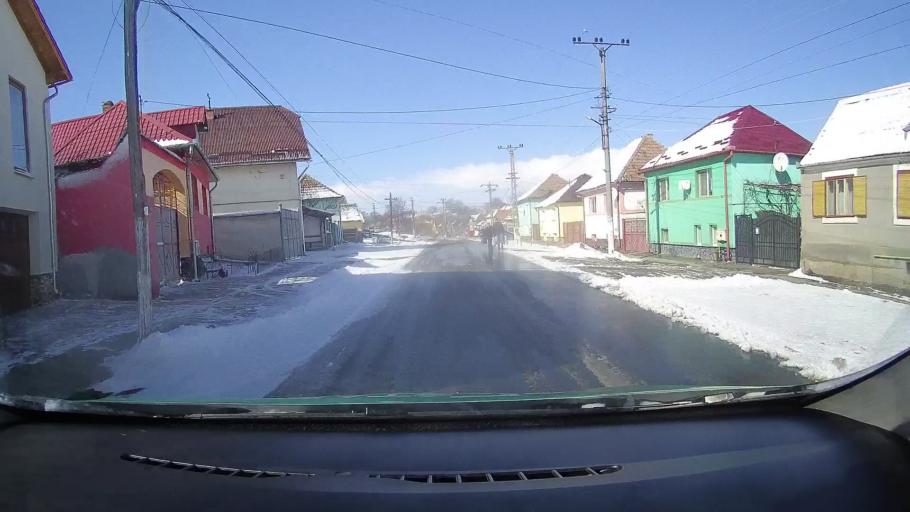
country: RO
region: Sibiu
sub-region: Comuna Rosia
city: Rosia
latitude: 45.8003
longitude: 24.2874
